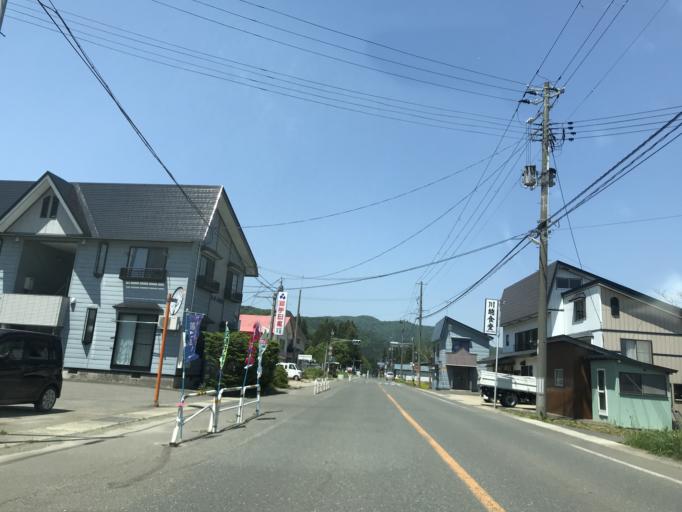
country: JP
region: Akita
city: Yokotemachi
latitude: 39.4319
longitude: 140.7509
